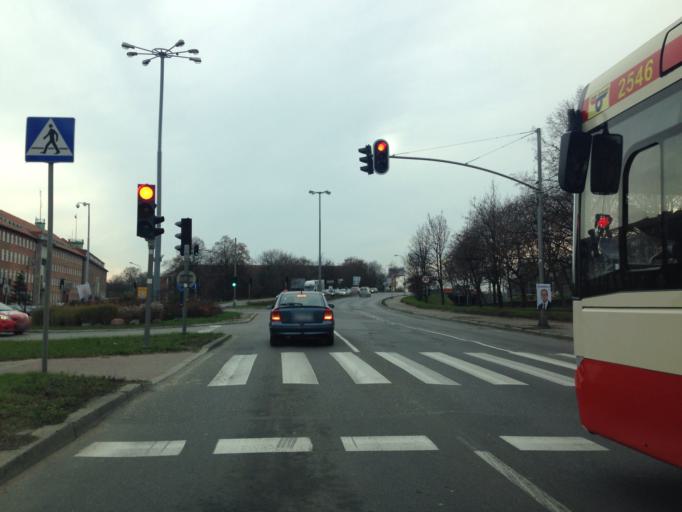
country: PL
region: Pomeranian Voivodeship
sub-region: Gdansk
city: Gdansk
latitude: 54.3456
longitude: 18.6453
